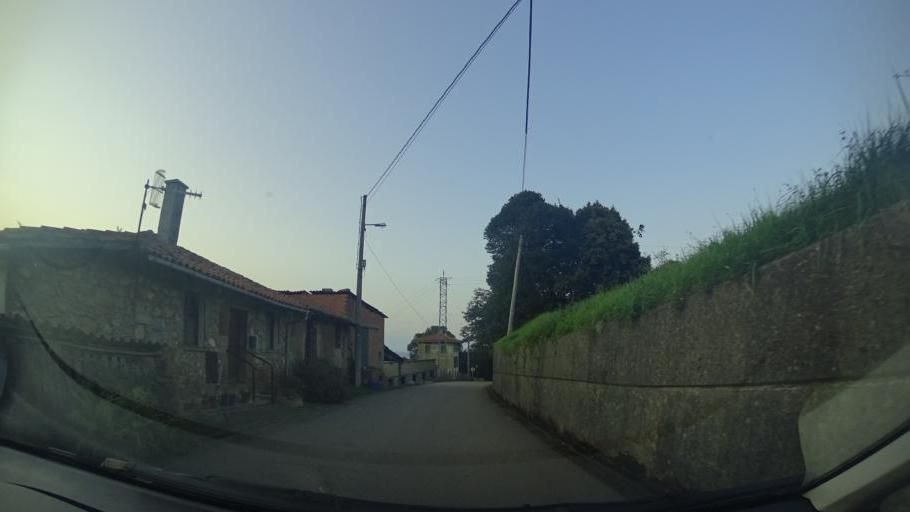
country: ES
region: Asturias
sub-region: Province of Asturias
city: Colunga
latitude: 43.4593
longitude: -5.2036
